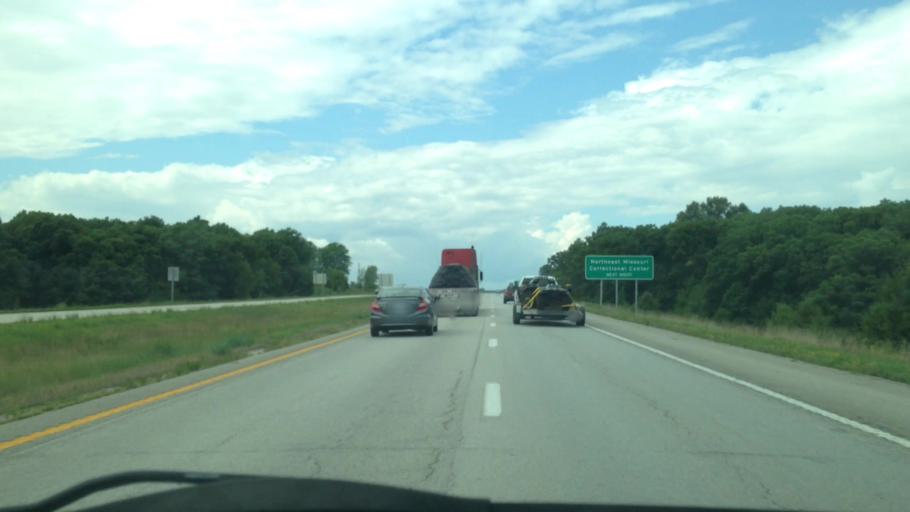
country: US
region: Missouri
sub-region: Pike County
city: Bowling Green
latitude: 39.3660
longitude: -91.2104
